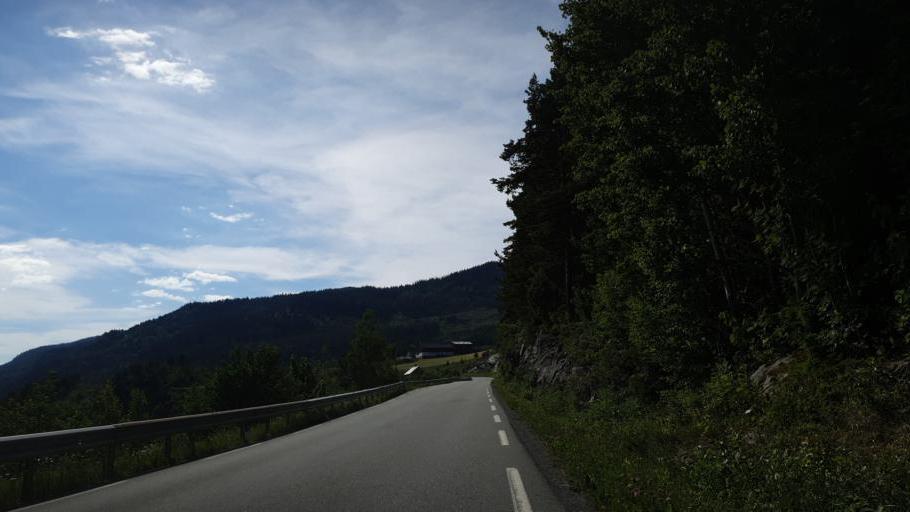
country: NO
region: Nord-Trondelag
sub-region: Leksvik
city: Leksvik
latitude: 63.6259
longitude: 10.5480
